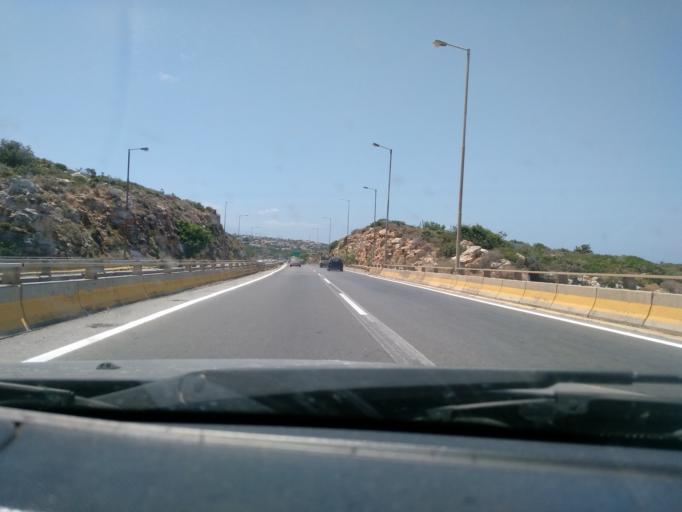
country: GR
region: Crete
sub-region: Nomos Rethymnis
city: Rethymno
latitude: 35.3584
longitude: 24.4595
